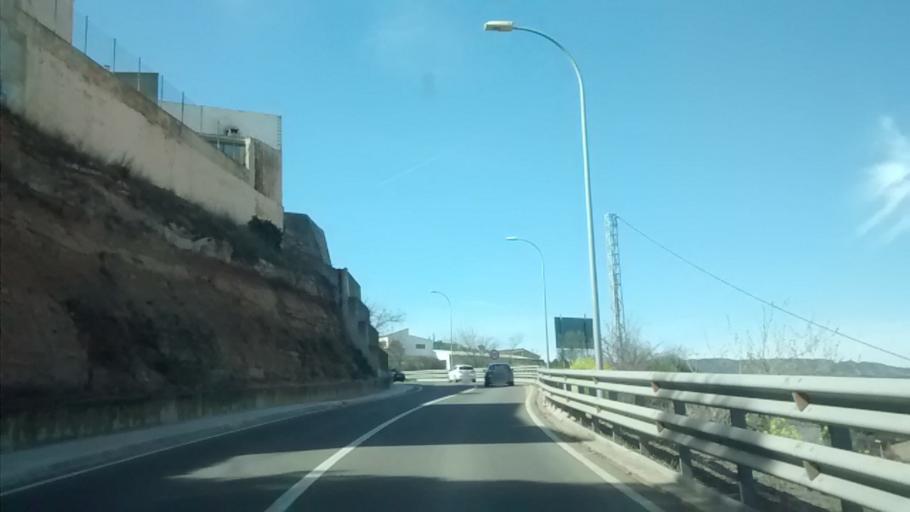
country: ES
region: Catalonia
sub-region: Provincia de Tarragona
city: Flix
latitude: 41.2290
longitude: 0.5445
